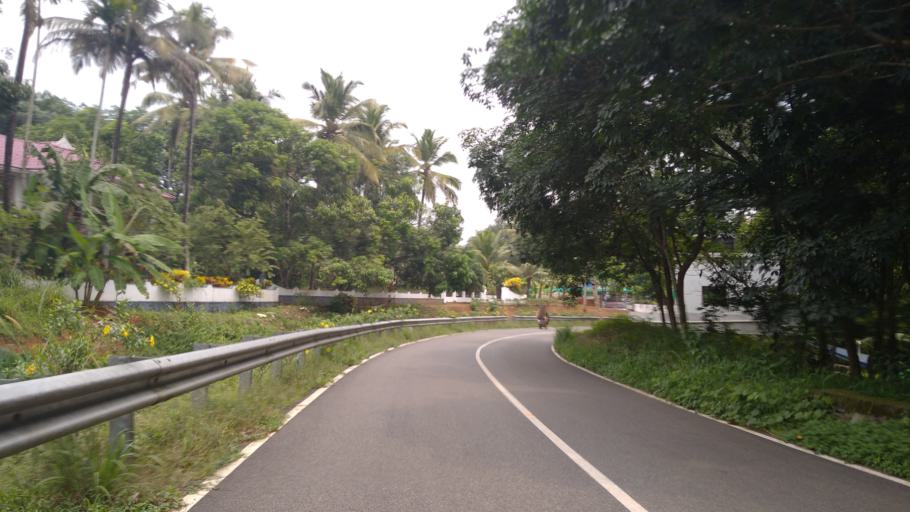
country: IN
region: Kerala
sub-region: Ernakulam
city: Ramamangalam
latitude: 10.0190
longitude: 76.4862
